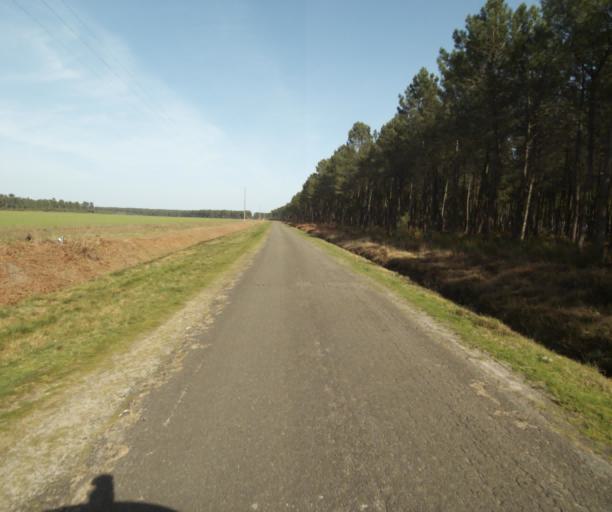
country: FR
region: Aquitaine
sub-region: Departement des Landes
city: Roquefort
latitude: 44.1653
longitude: -0.1999
